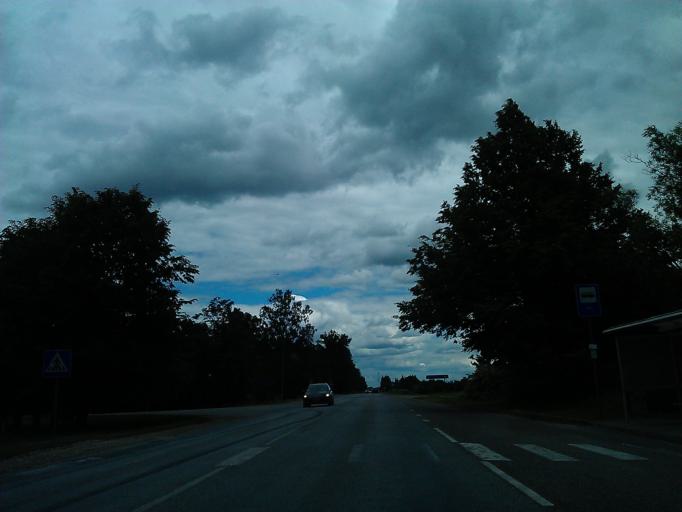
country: LV
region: Dobeles Rajons
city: Dobele
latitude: 56.6198
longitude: 23.4077
